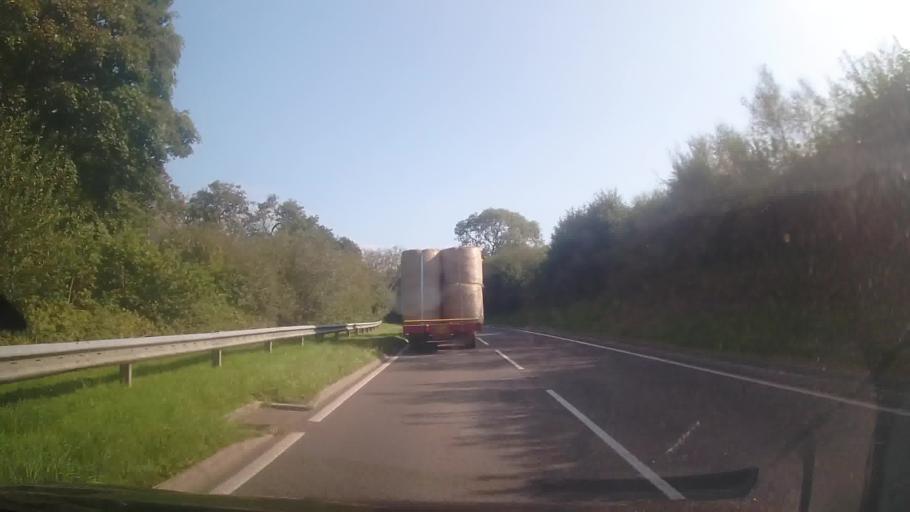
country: GB
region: Wales
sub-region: Pembrokeshire
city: Nevern
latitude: 52.0149
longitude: -4.7791
